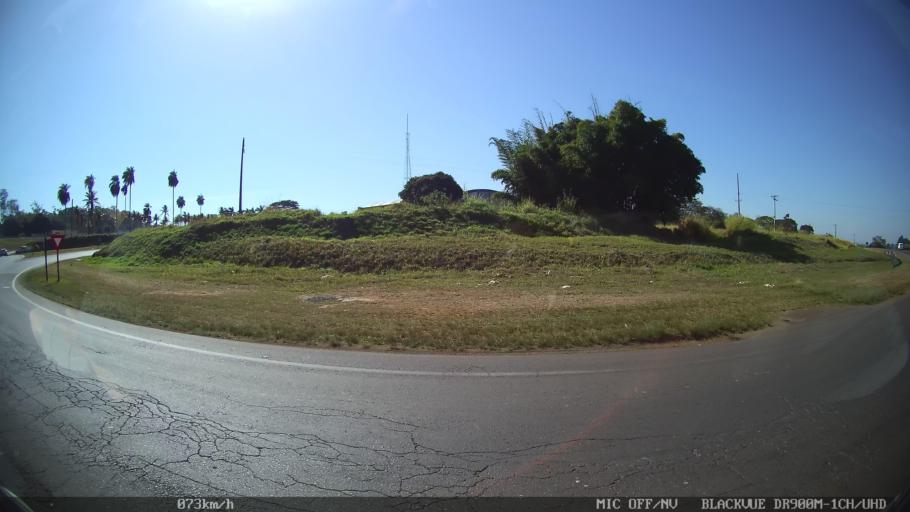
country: BR
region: Sao Paulo
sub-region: Batatais
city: Batatais
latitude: -20.9017
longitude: -47.6046
